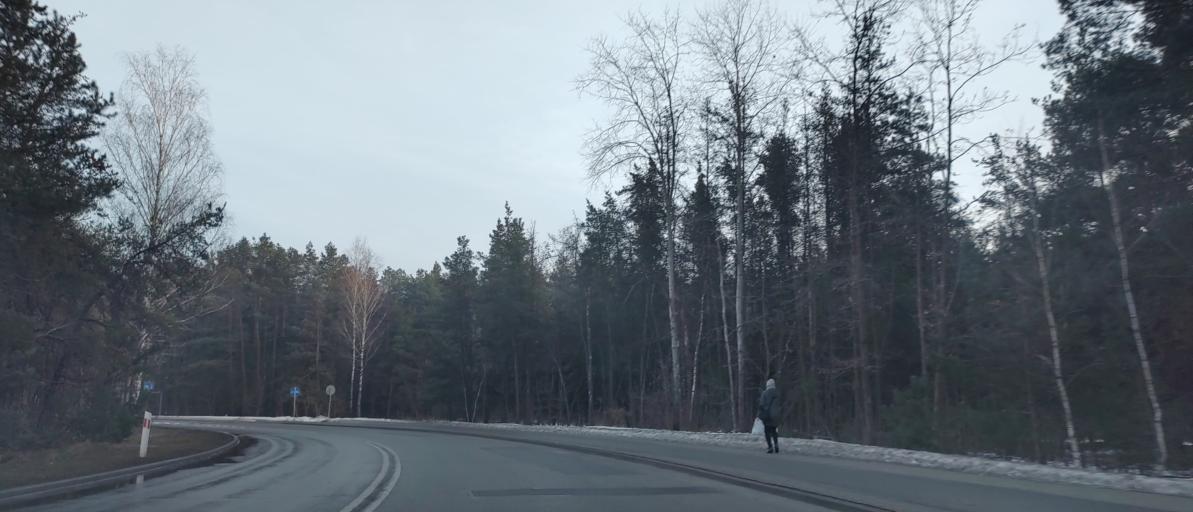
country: PL
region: Masovian Voivodeship
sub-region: Powiat bialobrzeski
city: Bialobrzegi
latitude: 51.6439
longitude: 20.9332
